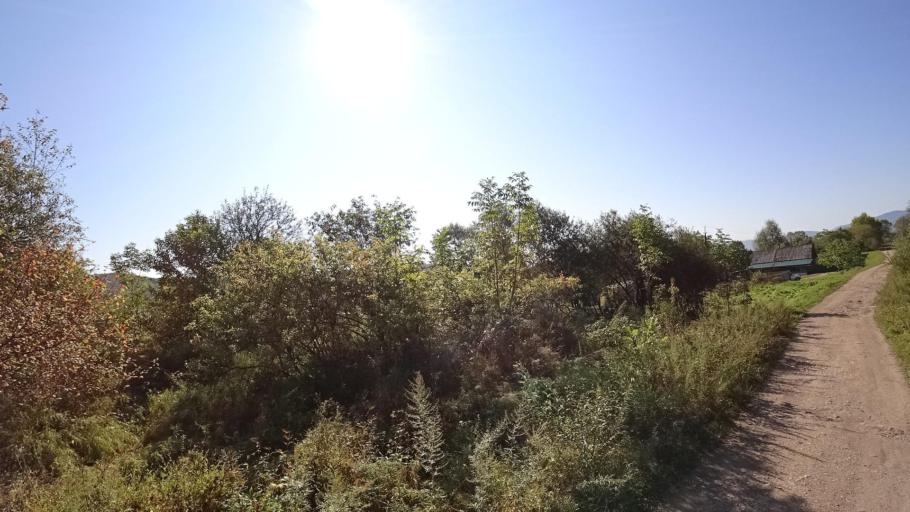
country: RU
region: Jewish Autonomous Oblast
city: Bira
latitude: 49.0070
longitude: 132.4749
